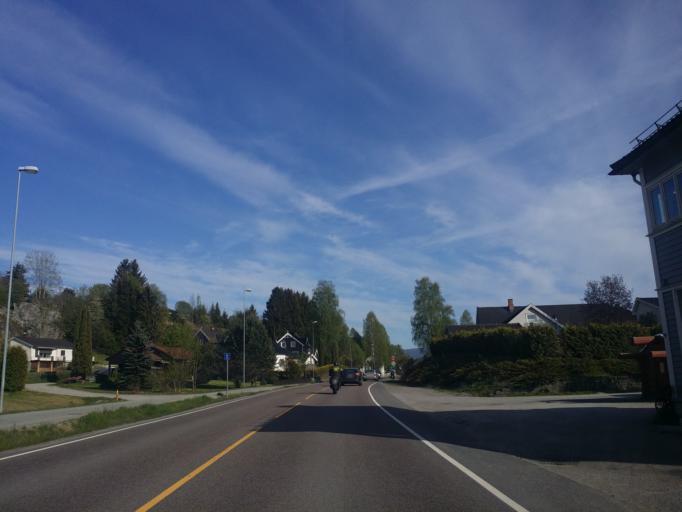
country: NO
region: Telemark
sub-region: Notodden
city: Notodden
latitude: 59.5751
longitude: 9.1949
